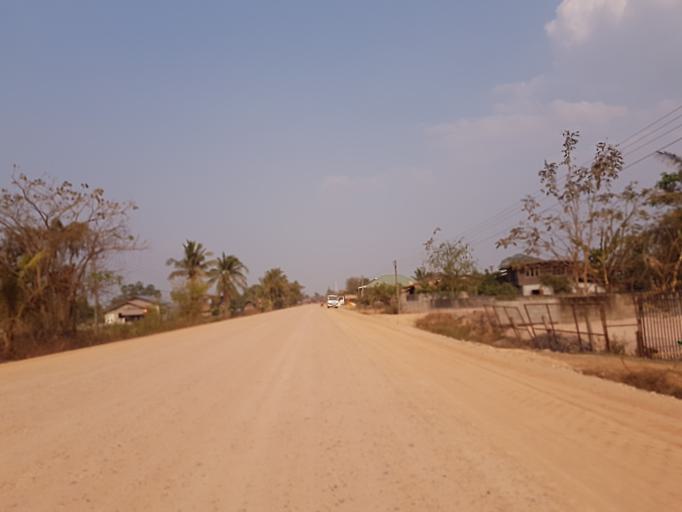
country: TH
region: Nong Khai
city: Nong Khai
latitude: 17.9825
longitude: 102.8883
